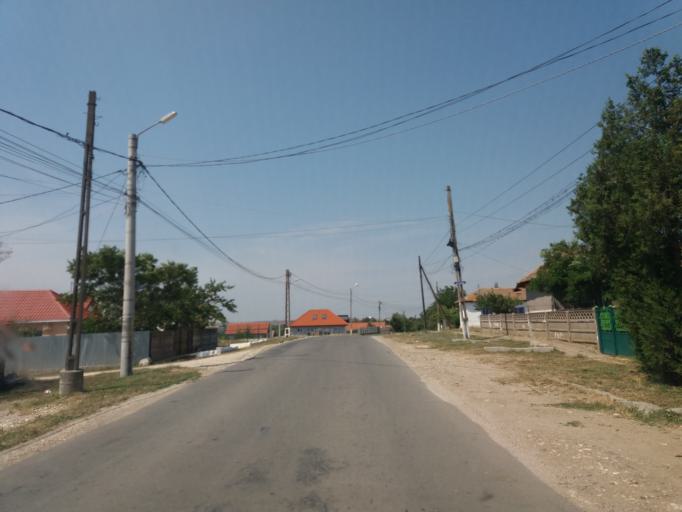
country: RO
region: Constanta
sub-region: Comuna Corbu
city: Corbu
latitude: 44.4050
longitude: 28.6615
